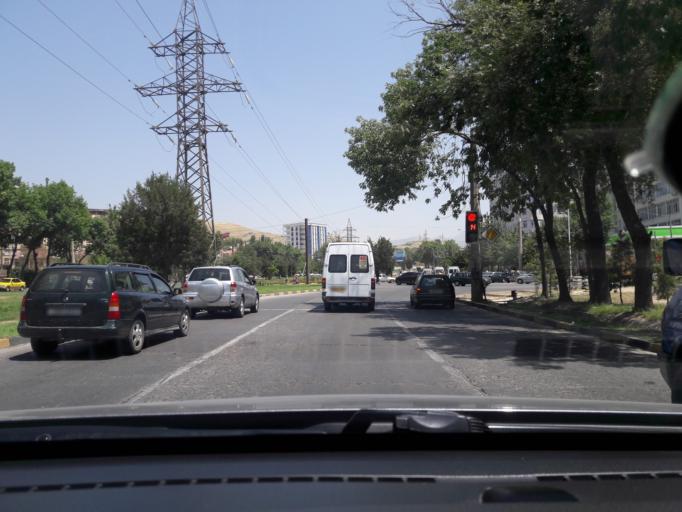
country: TJ
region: Dushanbe
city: Dushanbe
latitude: 38.5893
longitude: 68.7415
